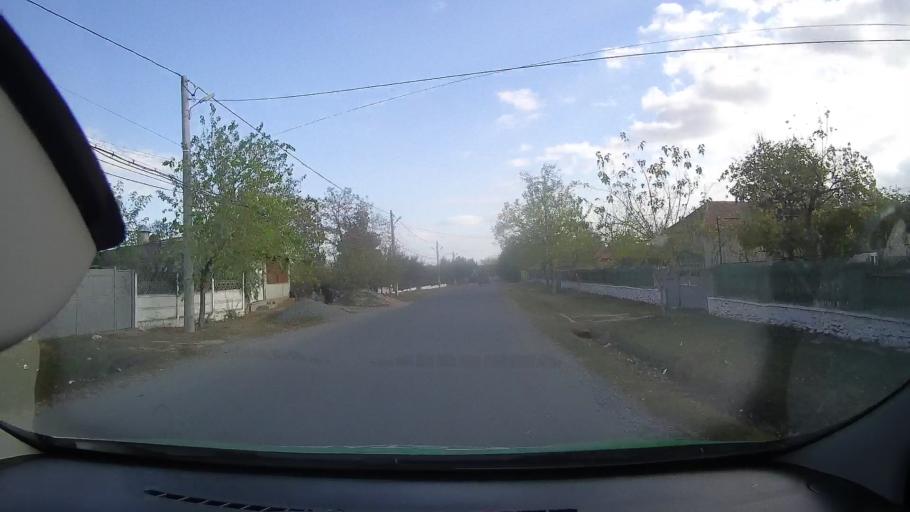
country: RO
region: Constanta
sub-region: Comuna Sacele
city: Sacele
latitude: 44.4881
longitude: 28.6414
